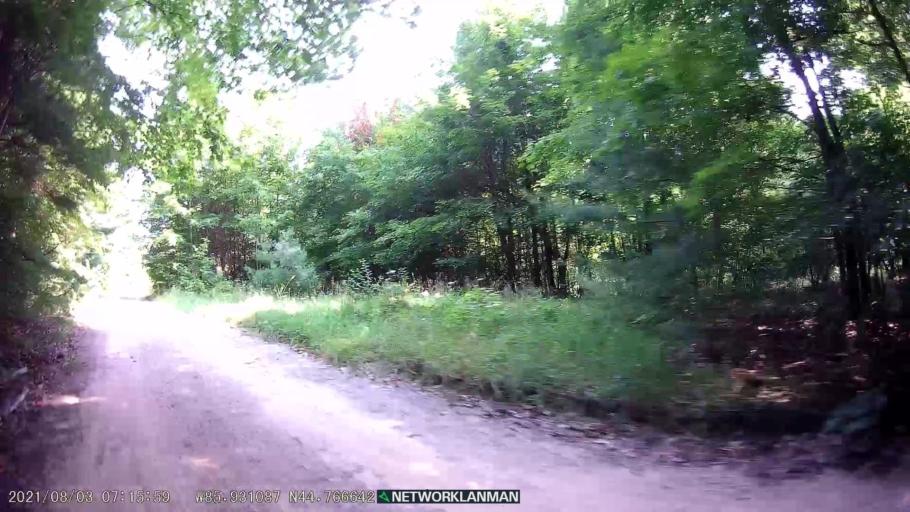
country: US
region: Michigan
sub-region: Benzie County
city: Beulah
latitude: 44.7667
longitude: -85.9313
